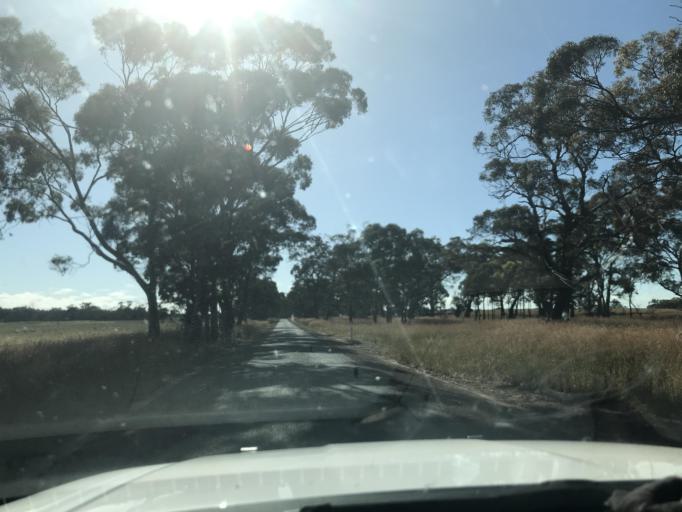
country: AU
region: Victoria
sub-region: Horsham
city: Horsham
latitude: -37.0252
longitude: 141.7047
